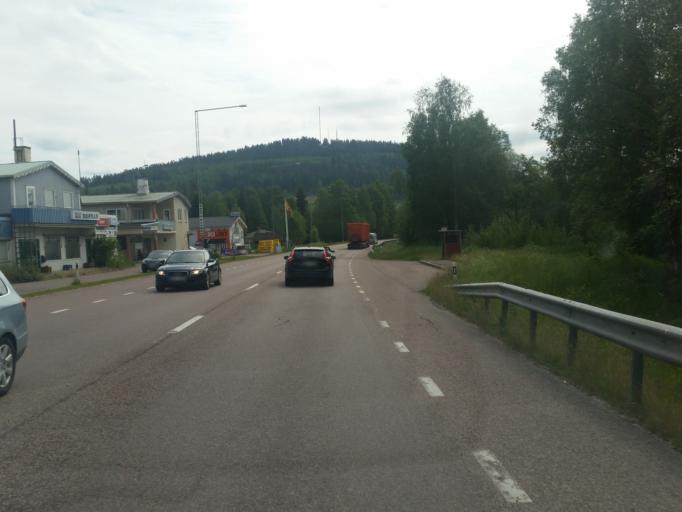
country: SE
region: Dalarna
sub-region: Gagnefs Kommun
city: Djuras
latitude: 60.5487
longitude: 15.2710
